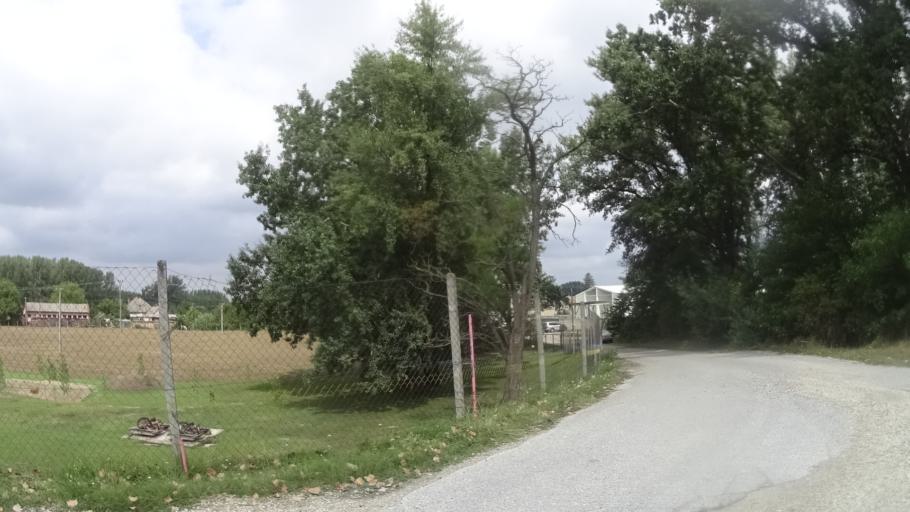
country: HU
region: Gyor-Moson-Sopron
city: Bony
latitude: 47.7461
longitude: 17.8778
